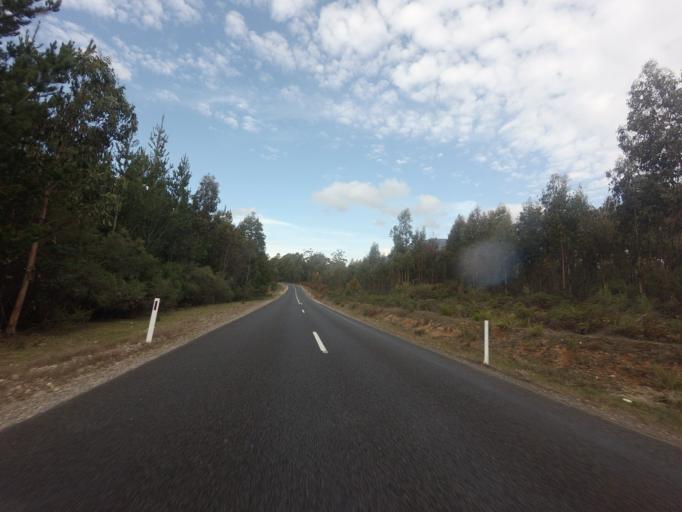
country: AU
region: Tasmania
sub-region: Meander Valley
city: Deloraine
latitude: -41.6125
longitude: 146.6869
